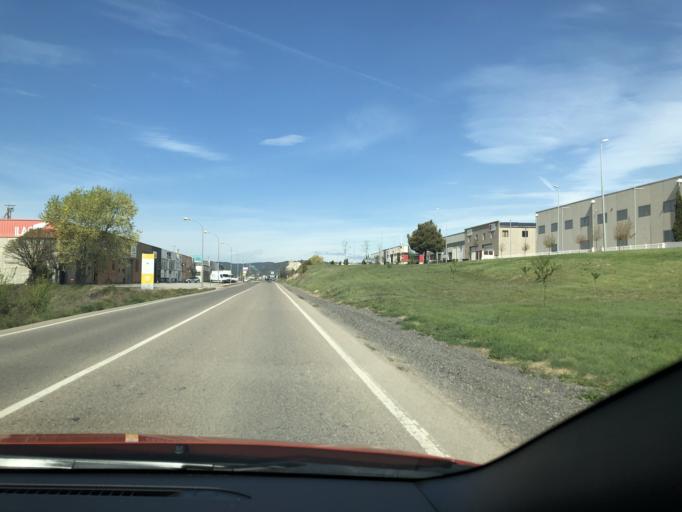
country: ES
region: Catalonia
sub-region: Provincia de Lleida
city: Olius
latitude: 41.9887
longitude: 1.5457
